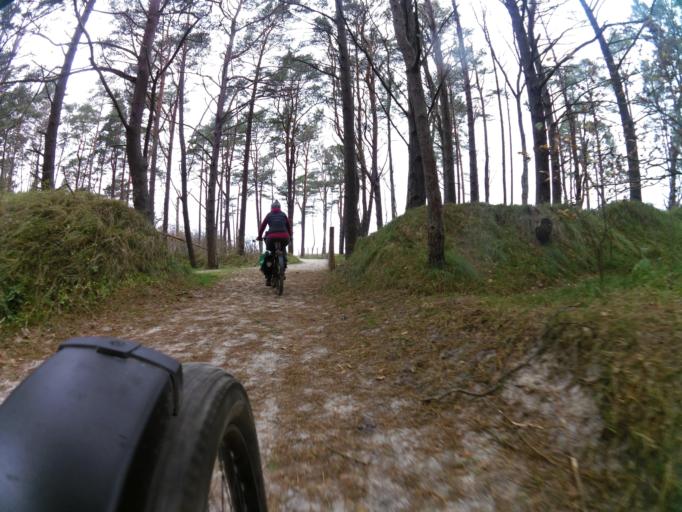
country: PL
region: Pomeranian Voivodeship
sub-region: Powiat pucki
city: Krokowa
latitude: 54.8311
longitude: 18.1243
